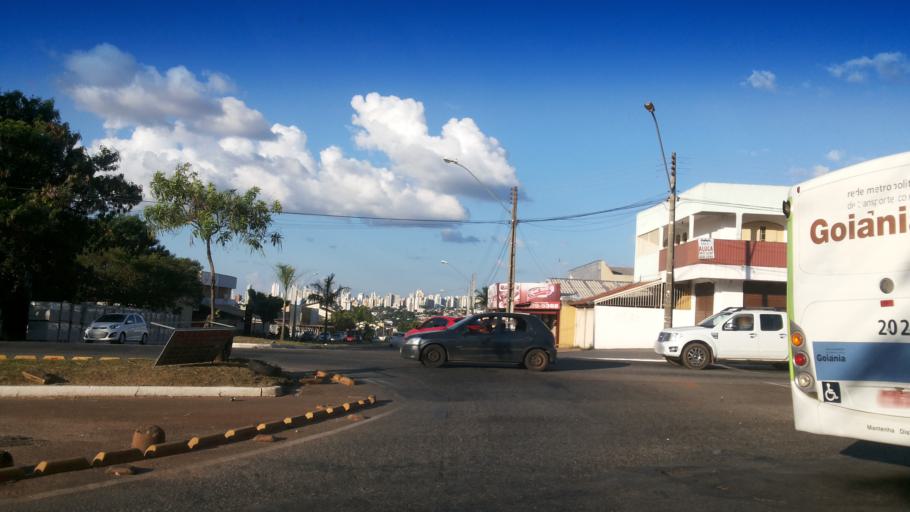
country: BR
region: Goias
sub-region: Goiania
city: Goiania
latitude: -16.7265
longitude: -49.3029
